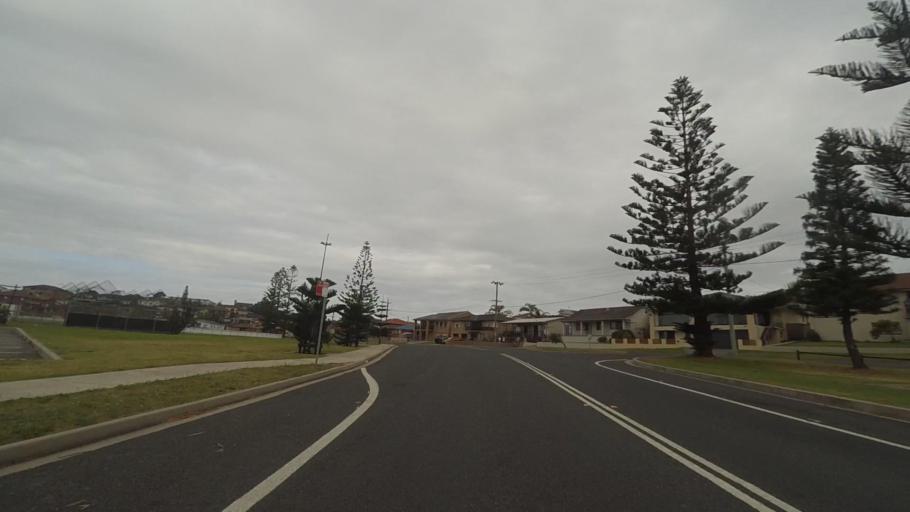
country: AU
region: New South Wales
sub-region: Wollongong
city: Port Kembla
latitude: -34.4908
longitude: 150.9105
